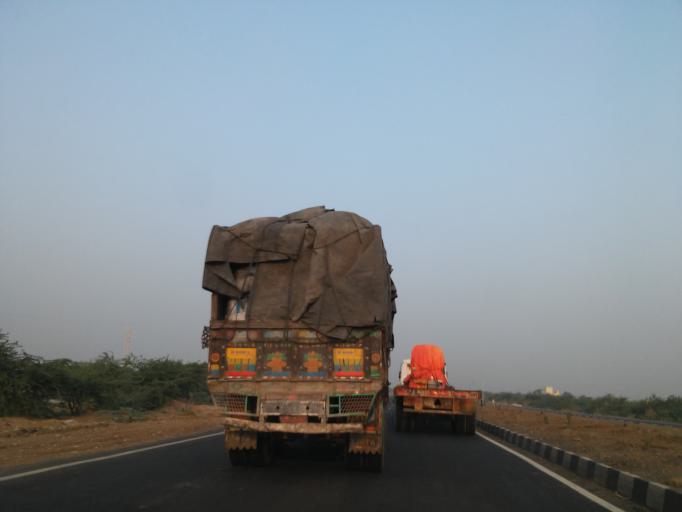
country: IN
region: Gujarat
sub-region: Kachchh
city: Rapar
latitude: 23.2440
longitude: 70.6713
